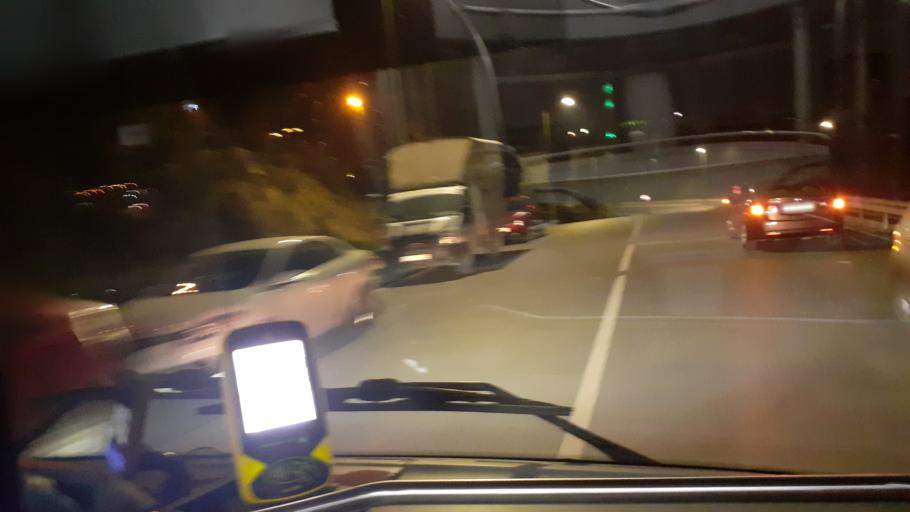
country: TR
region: Istanbul
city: Basaksehir
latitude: 41.0702
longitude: 28.7778
